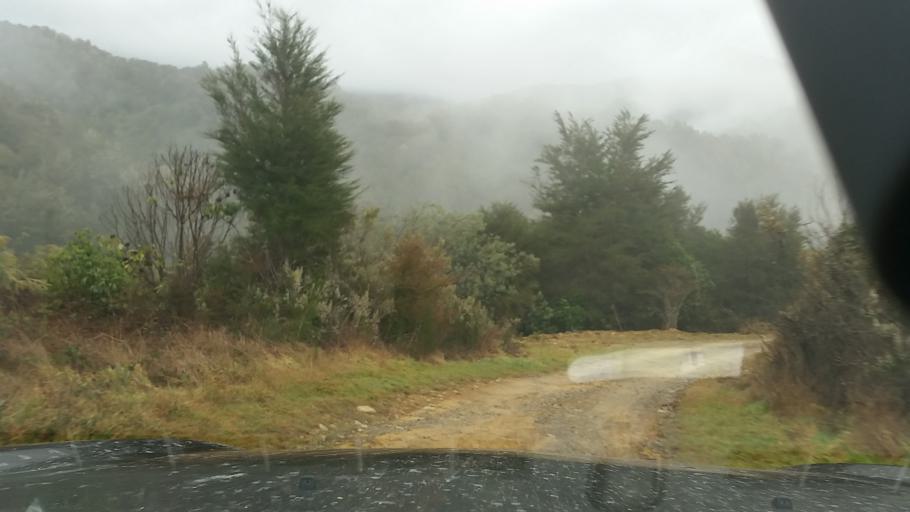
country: NZ
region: Nelson
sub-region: Nelson City
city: Nelson
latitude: -41.3768
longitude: 173.5951
